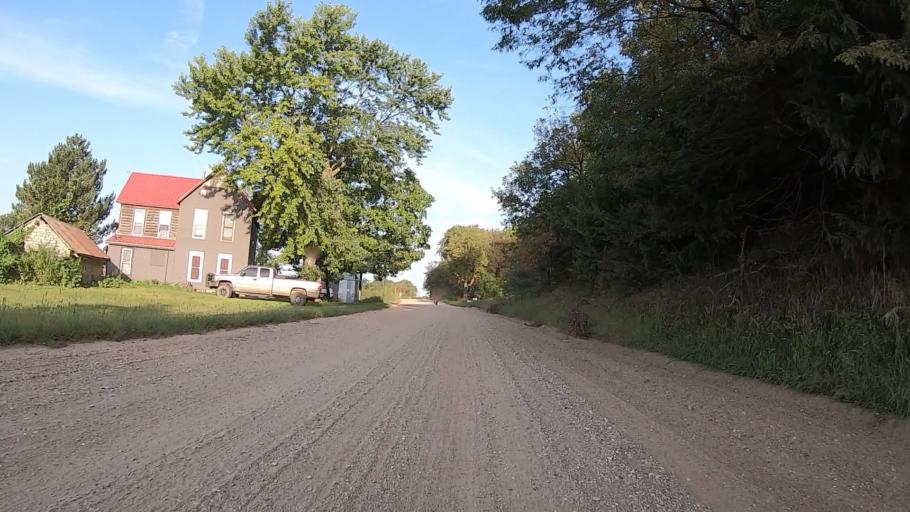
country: US
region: Kansas
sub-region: Marshall County
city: Blue Rapids
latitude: 39.7230
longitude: -96.7794
